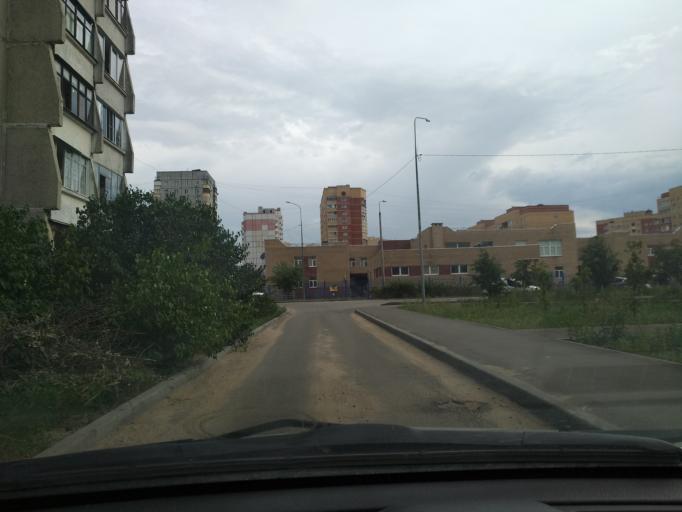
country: RU
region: Moskovskaya
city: Bykovo
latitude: 55.5957
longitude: 38.0905
